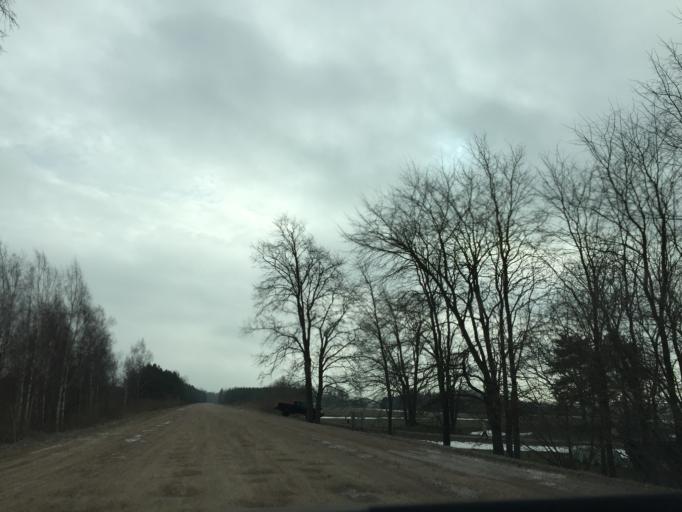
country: LV
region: Rundales
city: Pilsrundale
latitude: 56.5470
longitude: 23.9886
